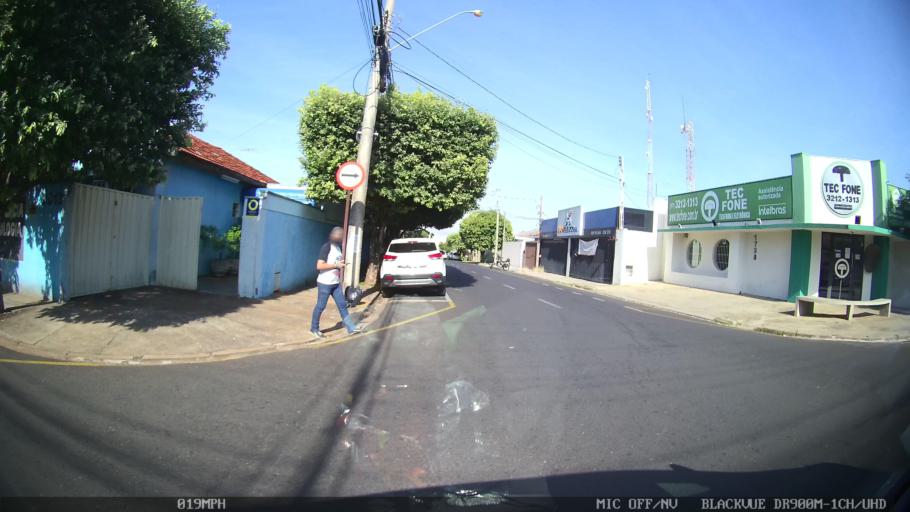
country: BR
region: Sao Paulo
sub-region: Sao Jose Do Rio Preto
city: Sao Jose do Rio Preto
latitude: -20.8059
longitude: -49.3926
